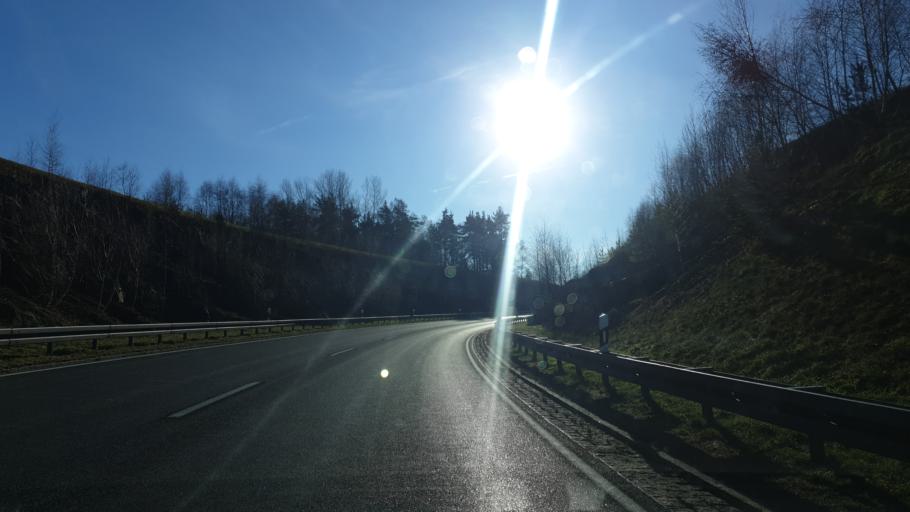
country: DE
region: Saxony
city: Bad Brambach
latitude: 50.2172
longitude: 12.3192
